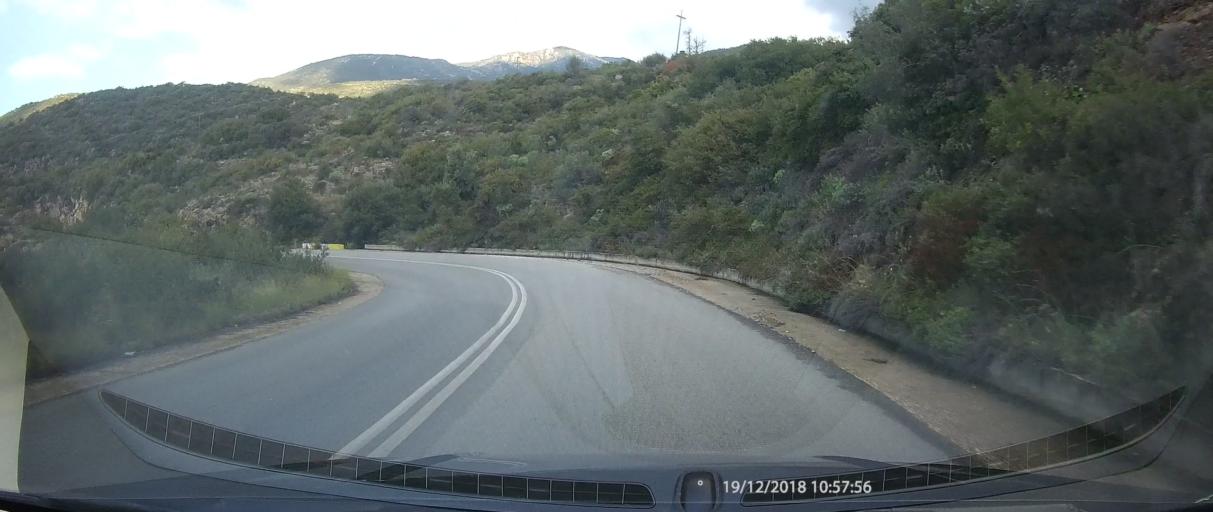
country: GR
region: Peloponnese
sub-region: Nomos Messinias
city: Kardamyli
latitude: 36.8971
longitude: 22.2366
